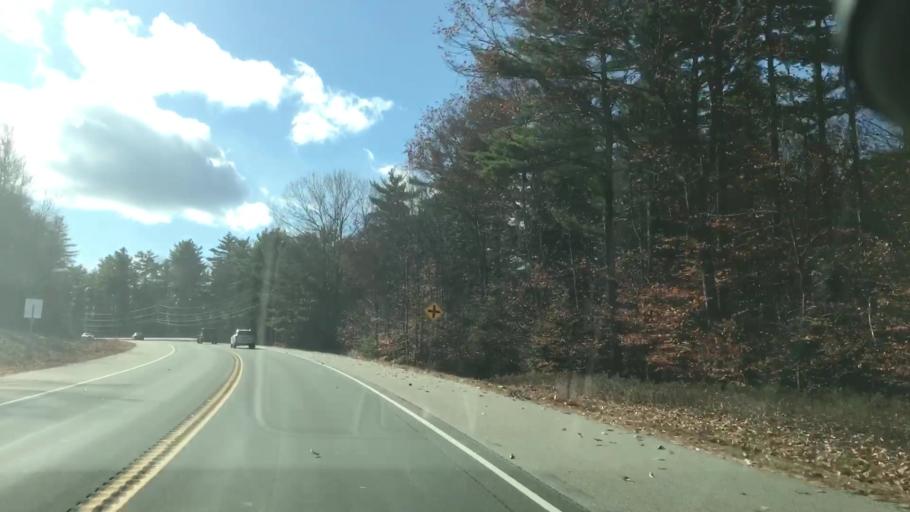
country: US
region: New Hampshire
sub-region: Carroll County
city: Wolfeboro
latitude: 43.5020
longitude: -71.2286
